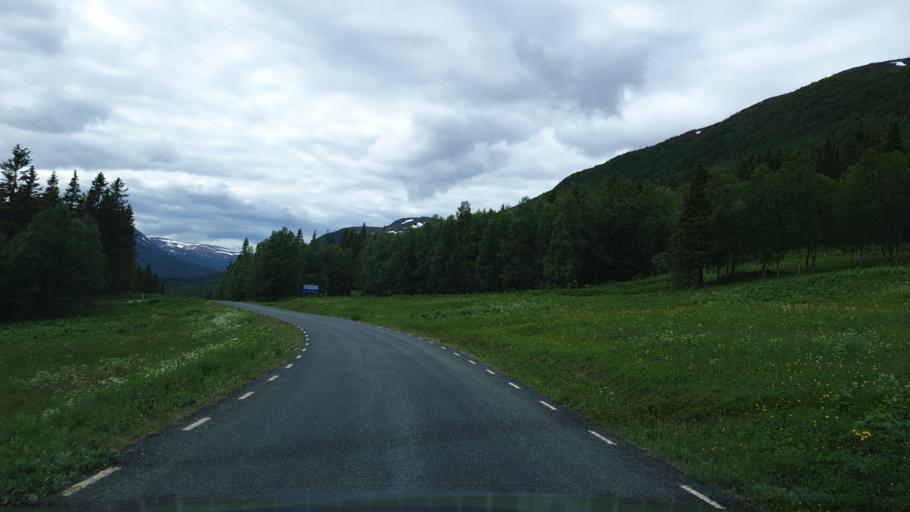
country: NO
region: Nordland
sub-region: Hattfjelldal
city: Hattfjelldal
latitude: 65.4462
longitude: 14.5258
